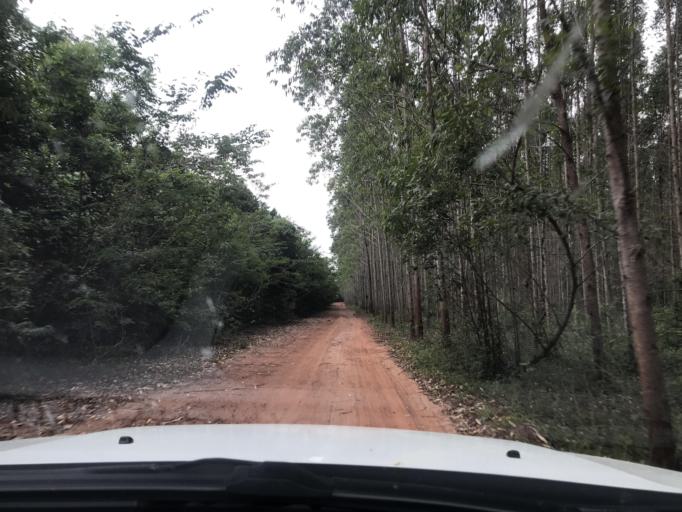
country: BR
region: Bahia
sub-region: Entre Rios
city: Entre Rios
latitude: -12.1082
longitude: -38.1855
